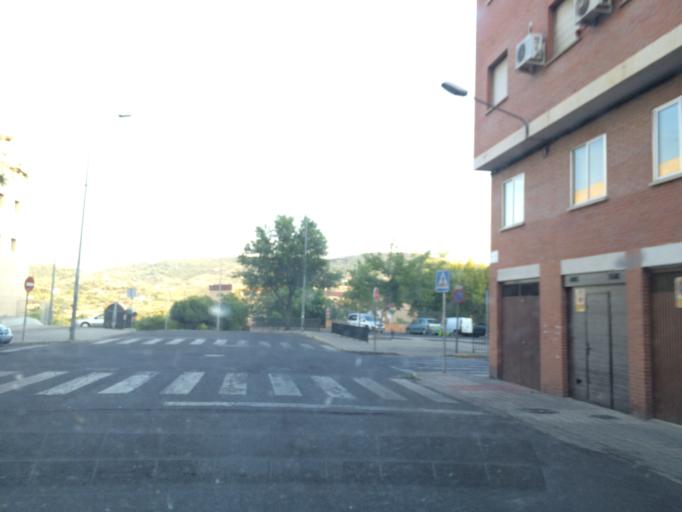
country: ES
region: Extremadura
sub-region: Provincia de Caceres
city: Plasencia
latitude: 40.0377
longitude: -6.0808
